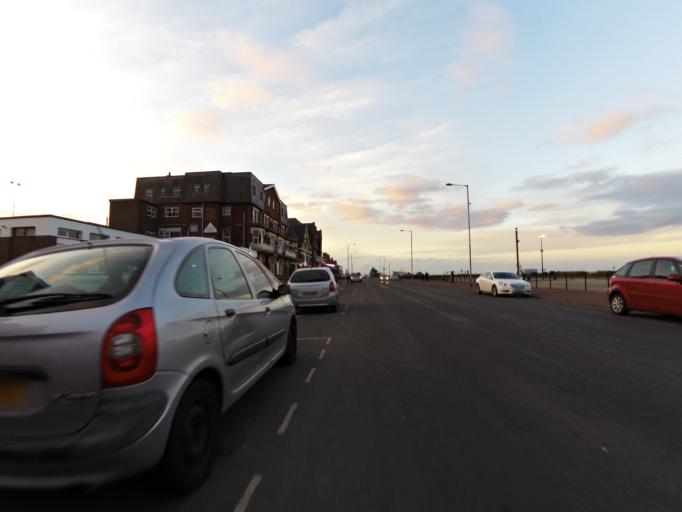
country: GB
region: England
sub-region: Norfolk
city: Great Yarmouth
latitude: 52.6120
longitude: 1.7377
